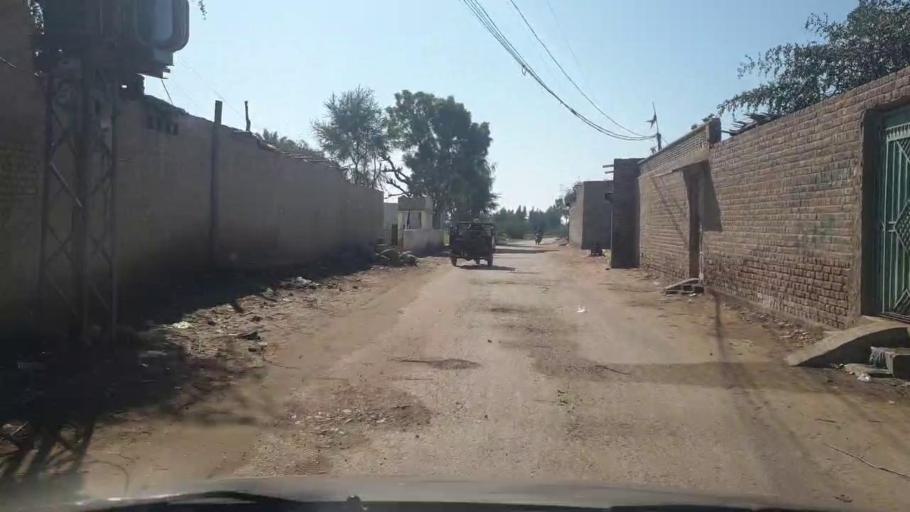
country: PK
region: Sindh
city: Bozdar
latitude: 27.1058
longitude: 68.6328
